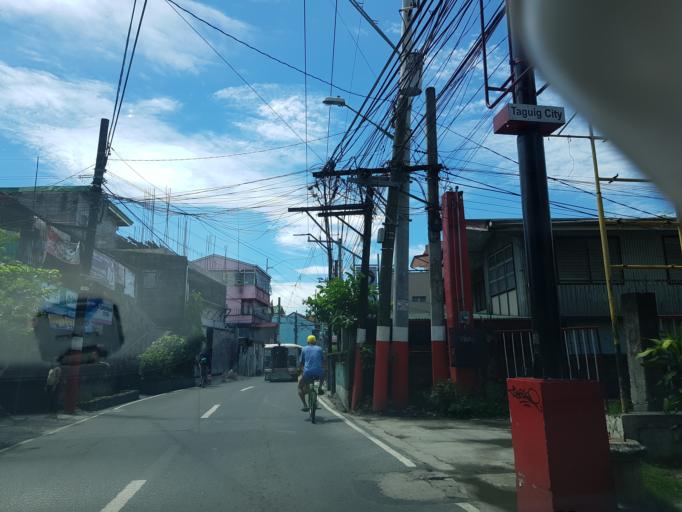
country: PH
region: Calabarzon
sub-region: Province of Rizal
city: Taguig
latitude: 14.5264
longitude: 121.0727
